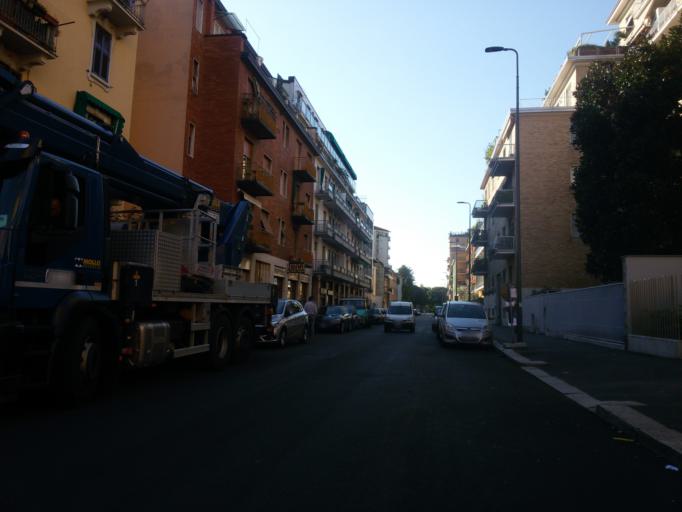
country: IT
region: Lombardy
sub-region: Citta metropolitana di Milano
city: Romano Banco
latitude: 45.4630
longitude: 9.1404
